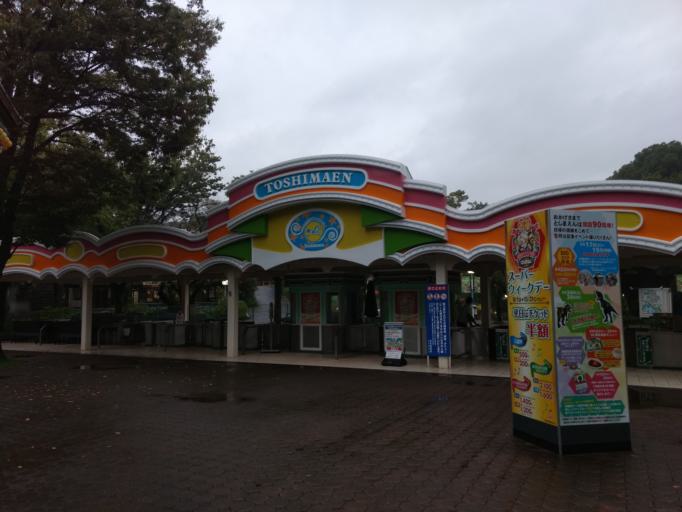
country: JP
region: Saitama
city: Wako
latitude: 35.7432
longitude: 139.6475
